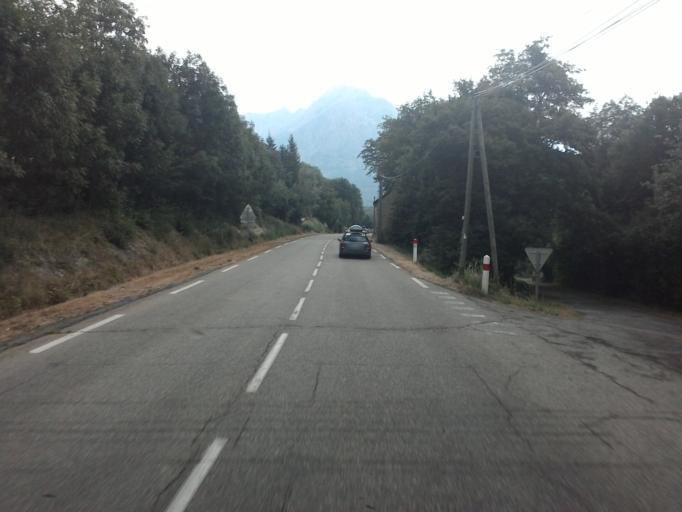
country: FR
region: Provence-Alpes-Cote d'Azur
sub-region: Departement des Hautes-Alpes
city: Saint-Bonnet-en-Champsaur
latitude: 44.7777
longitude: 5.9862
